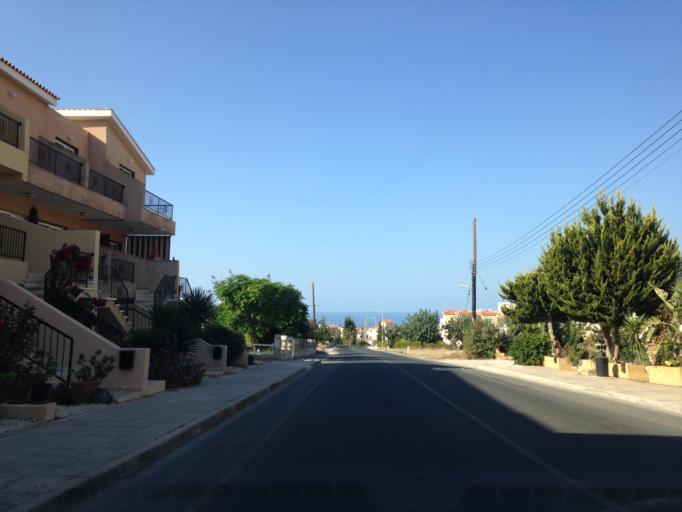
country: CY
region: Pafos
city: Pegeia
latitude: 34.8778
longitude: 32.3737
